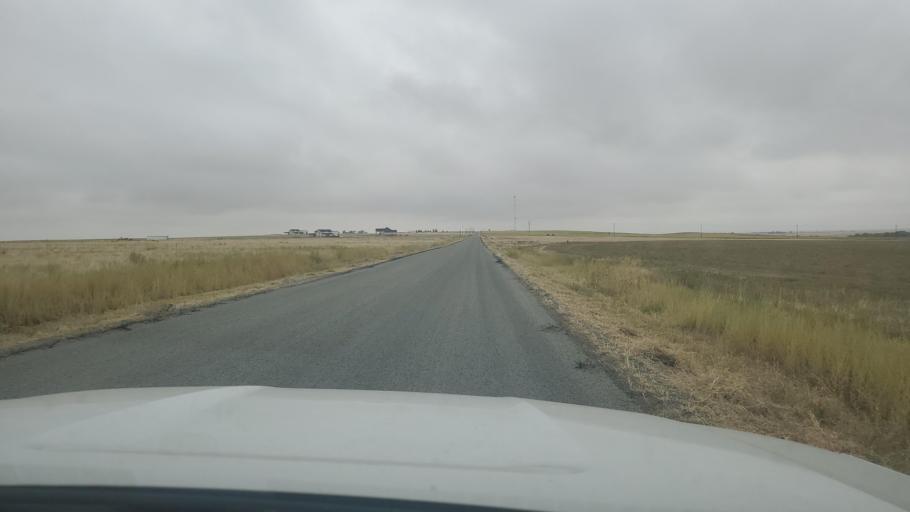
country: US
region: Colorado
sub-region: Weld County
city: Lochbuie
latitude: 39.9326
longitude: -104.6028
